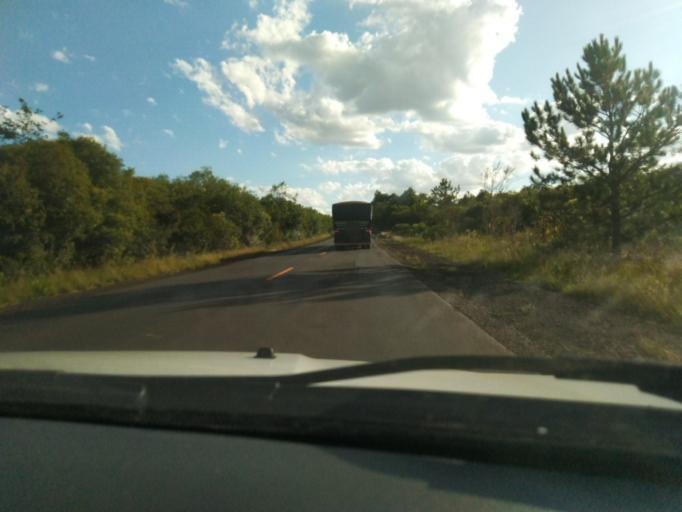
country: AR
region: Corrientes
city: Garruchos
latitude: -28.5429
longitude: -55.5522
